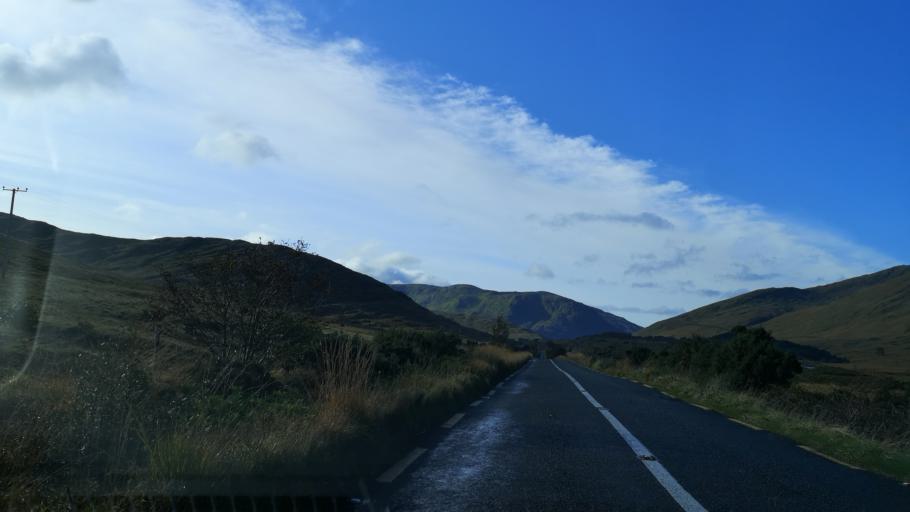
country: IE
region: Connaught
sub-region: Maigh Eo
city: Westport
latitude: 53.6237
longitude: -9.6457
